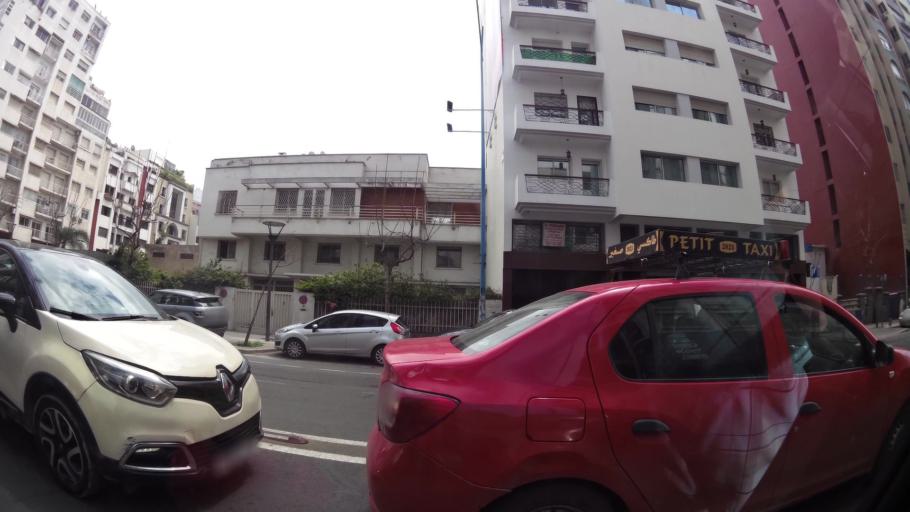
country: MA
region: Grand Casablanca
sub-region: Casablanca
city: Casablanca
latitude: 33.5918
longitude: -7.6346
